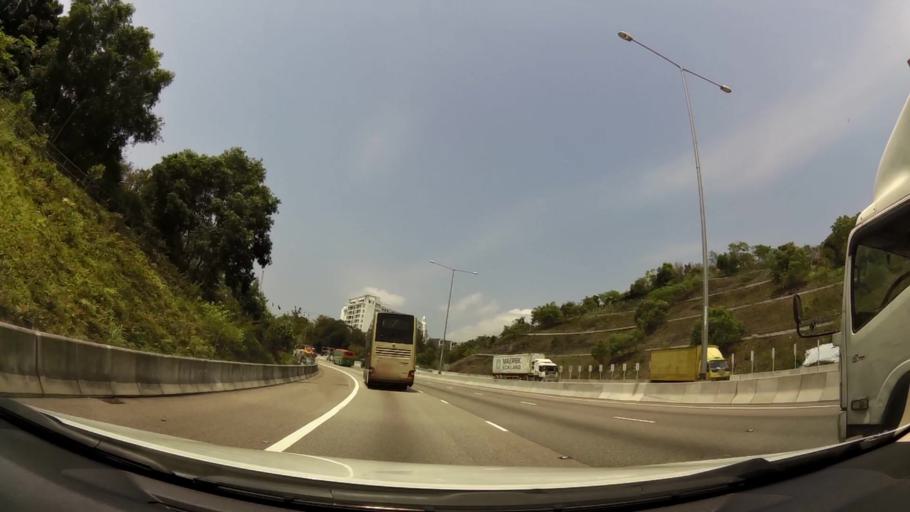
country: HK
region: Tuen Mun
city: Tuen Mun
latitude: 22.3759
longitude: 113.9949
